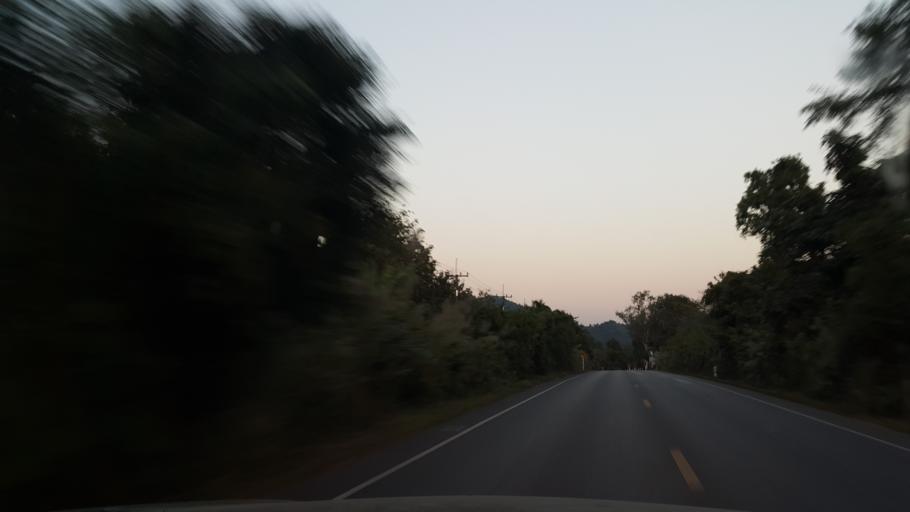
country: TH
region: Phrae
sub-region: Amphoe Wang Chin
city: Wang Chin
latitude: 17.9660
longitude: 99.6135
